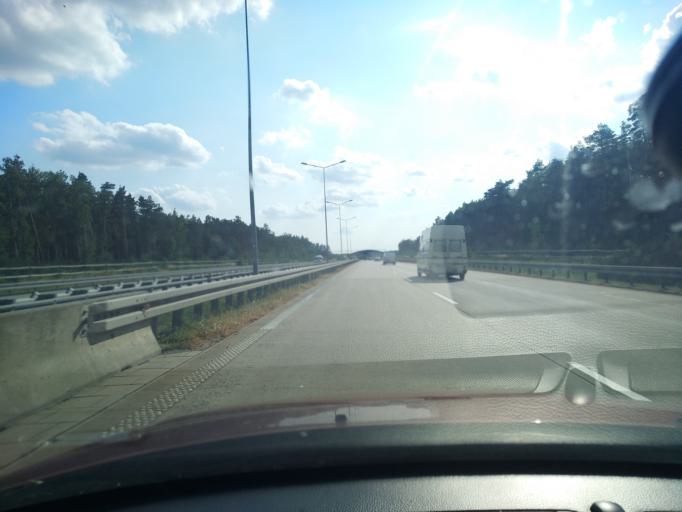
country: PL
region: Lower Silesian Voivodeship
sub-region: Powiat boleslawiecki
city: Nowogrodziec
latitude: 51.2441
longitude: 15.3402
